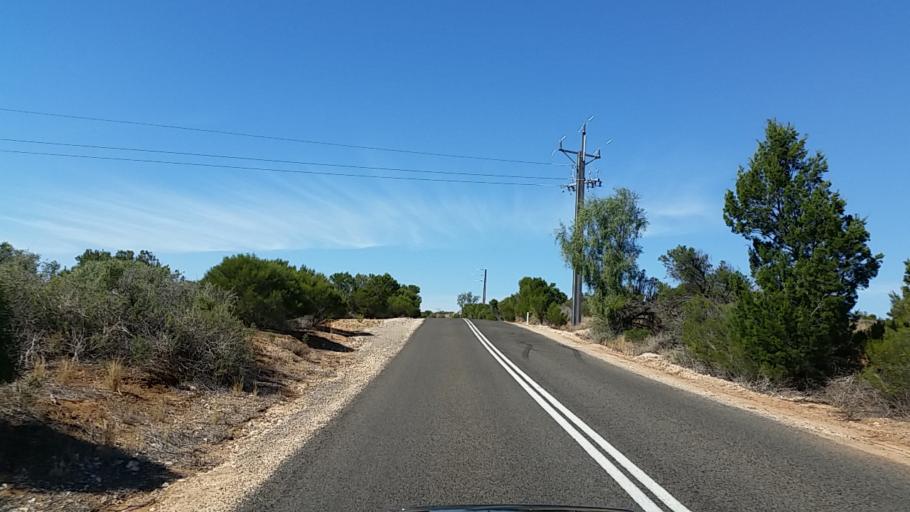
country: AU
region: South Australia
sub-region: Mid Murray
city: Mannum
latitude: -34.7451
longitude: 139.5408
